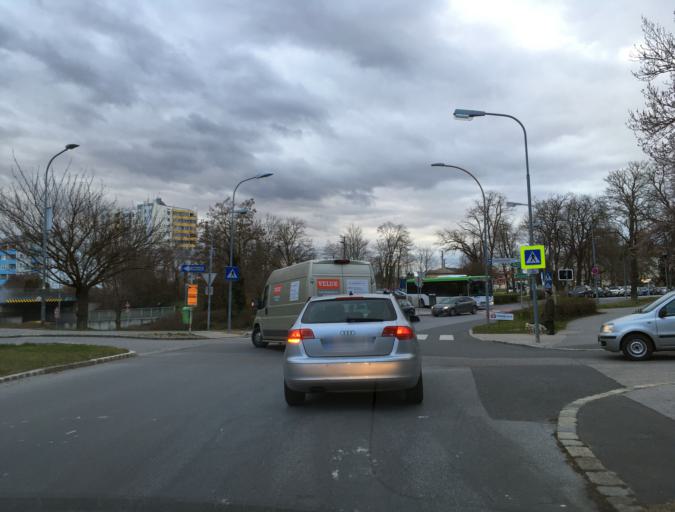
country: AT
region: Lower Austria
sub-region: Politischer Bezirk Korneuburg
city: Korneuburg
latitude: 48.3415
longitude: 16.3311
